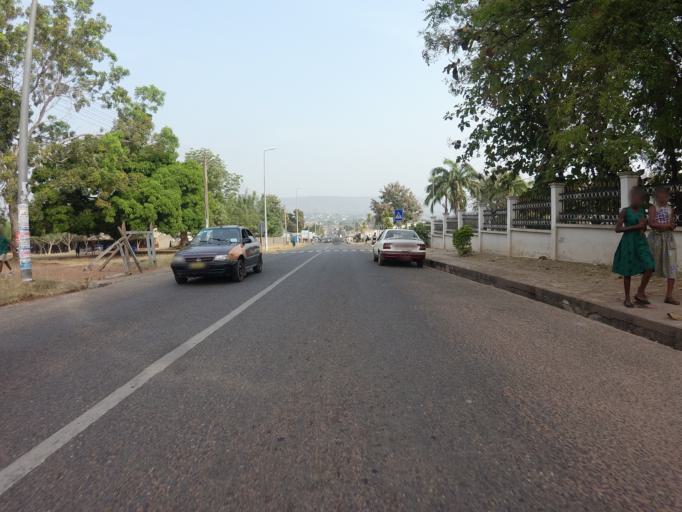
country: GH
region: Volta
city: Ho
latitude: 6.6028
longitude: 0.4752
